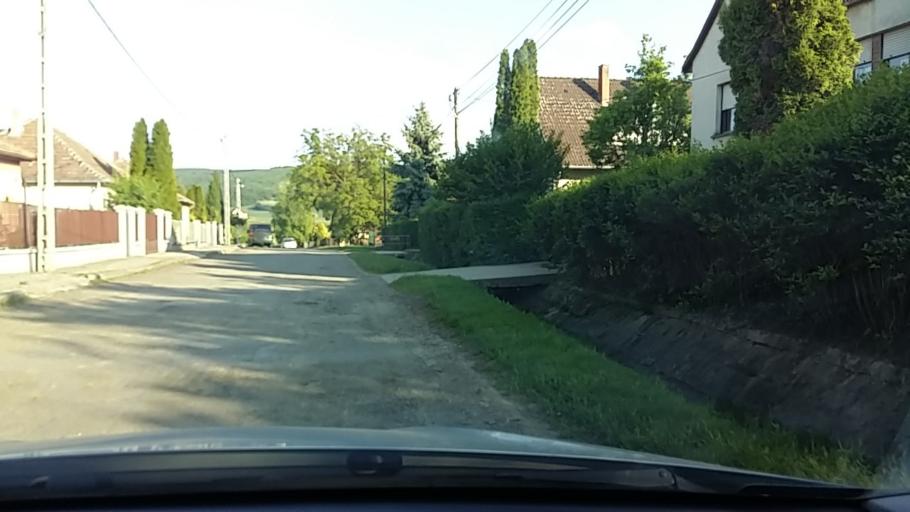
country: HU
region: Pest
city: Kosd
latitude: 47.7982
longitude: 19.2508
